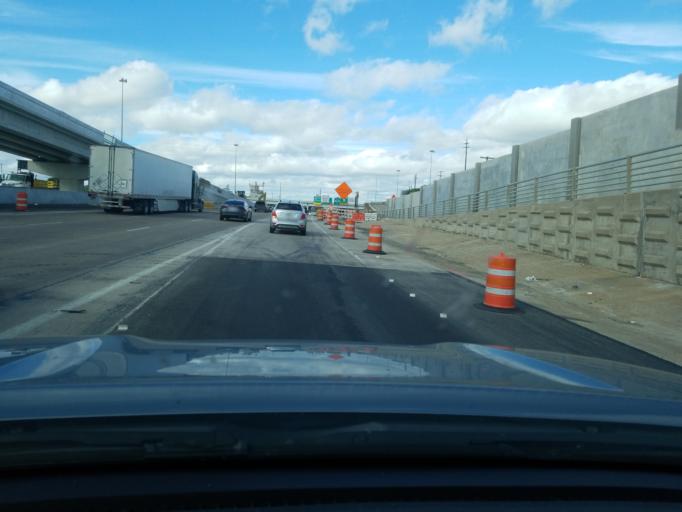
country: US
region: Texas
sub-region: Tarrant County
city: Fort Worth
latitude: 32.7519
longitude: -97.3196
